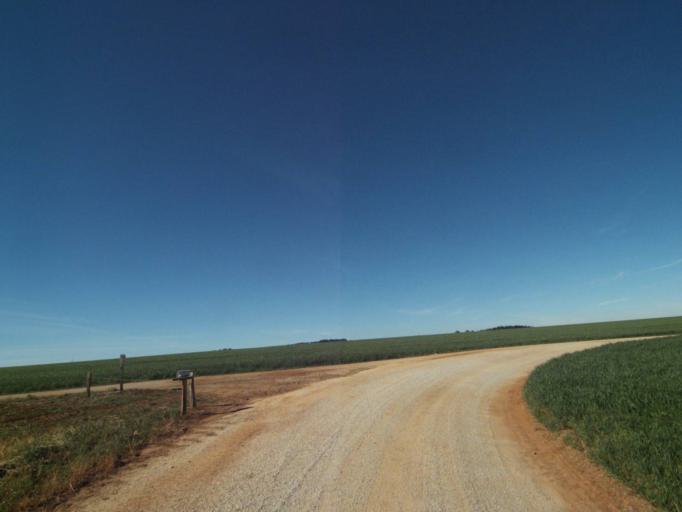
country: BR
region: Parana
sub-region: Tibagi
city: Tibagi
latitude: -24.5383
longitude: -50.3027
